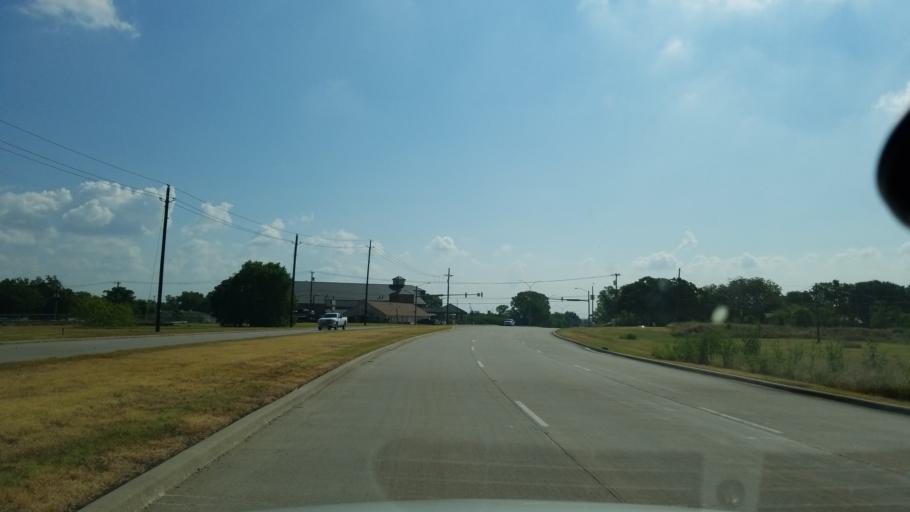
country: US
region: Texas
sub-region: Tarrant County
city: Bedford
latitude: 32.8103
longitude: -97.1247
